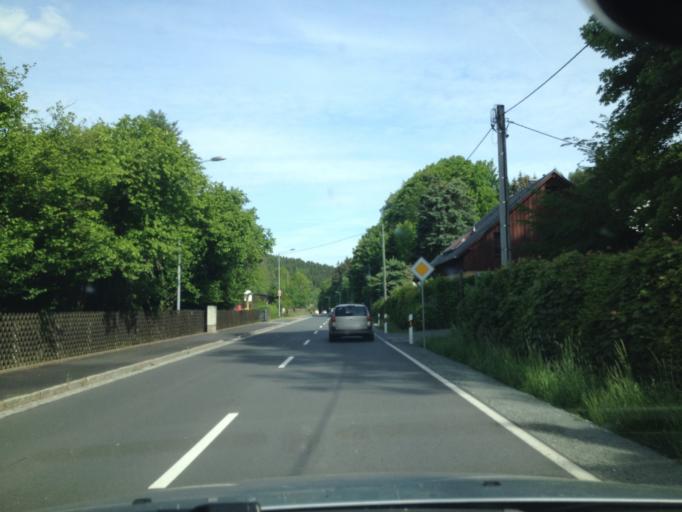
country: DE
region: Saxony
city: Ehrenfriedersdorf
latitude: 50.6563
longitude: 12.9713
